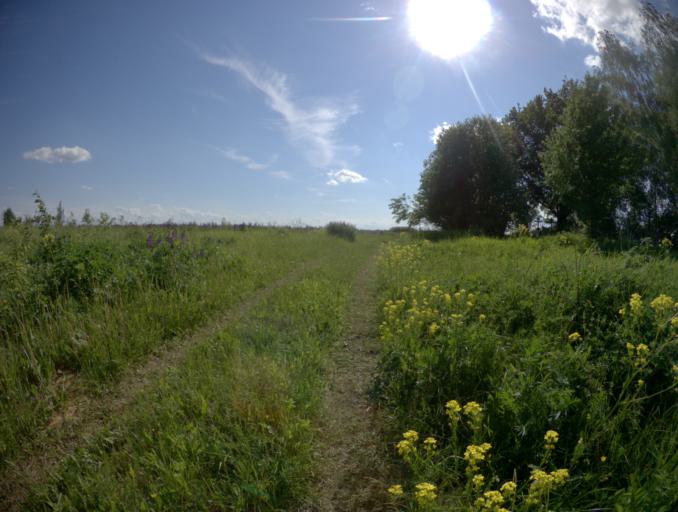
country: RU
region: Vladimir
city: Suzdal'
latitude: 56.3318
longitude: 40.4389
